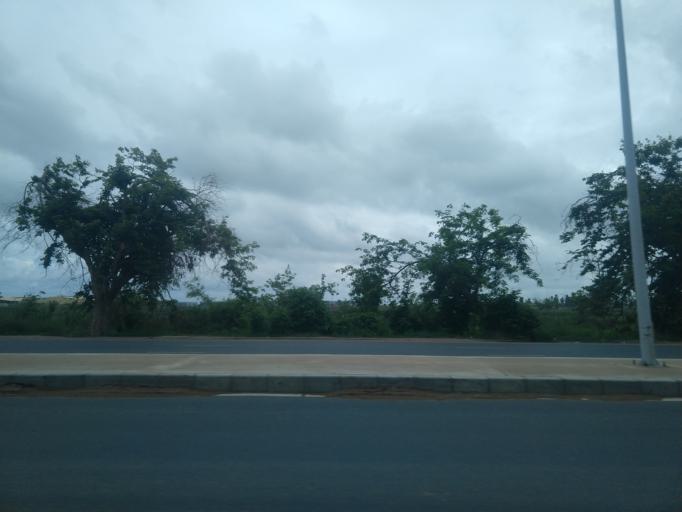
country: MZ
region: Sofala
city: Beira
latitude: -19.7878
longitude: 34.8748
